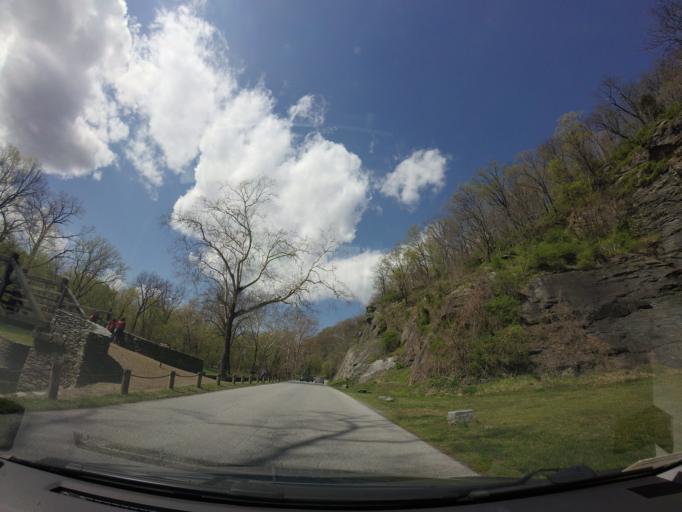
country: US
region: West Virginia
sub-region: Jefferson County
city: Bolivar
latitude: 39.3224
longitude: -77.7362
